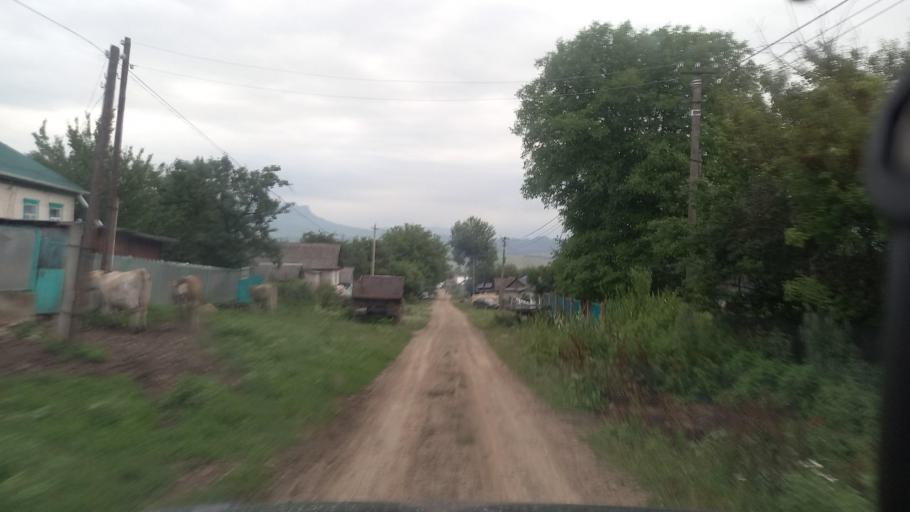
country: RU
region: Karachayevo-Cherkesiya
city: Pregradnaya
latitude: 43.9515
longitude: 41.1720
